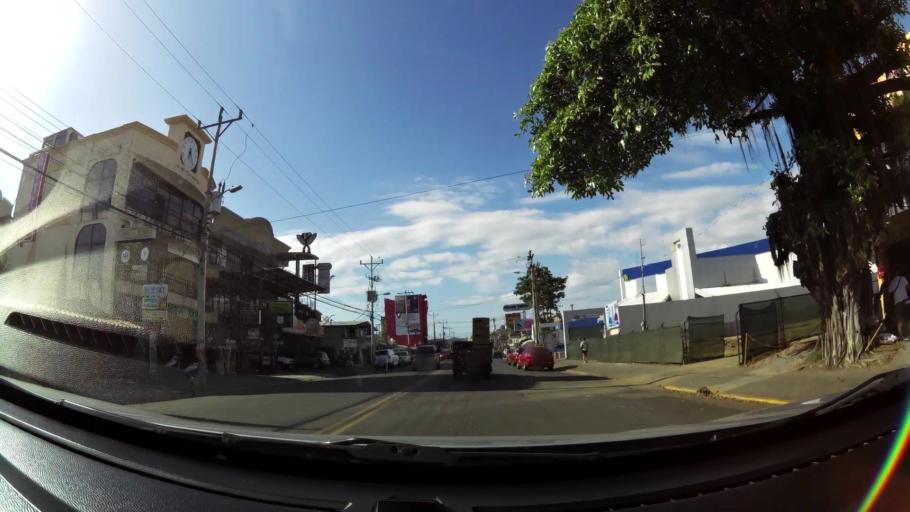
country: CR
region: Puntarenas
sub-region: Canton de Garabito
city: Jaco
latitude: 9.6132
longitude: -84.6269
